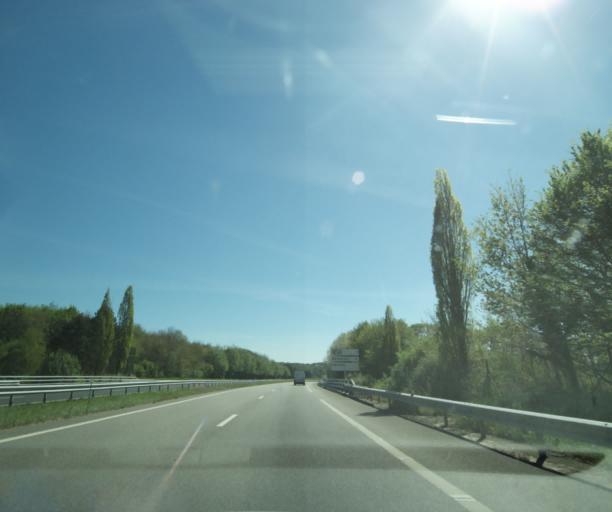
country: FR
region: Limousin
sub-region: Departement de la Correze
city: Uzerche
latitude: 45.3879
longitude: 1.5743
